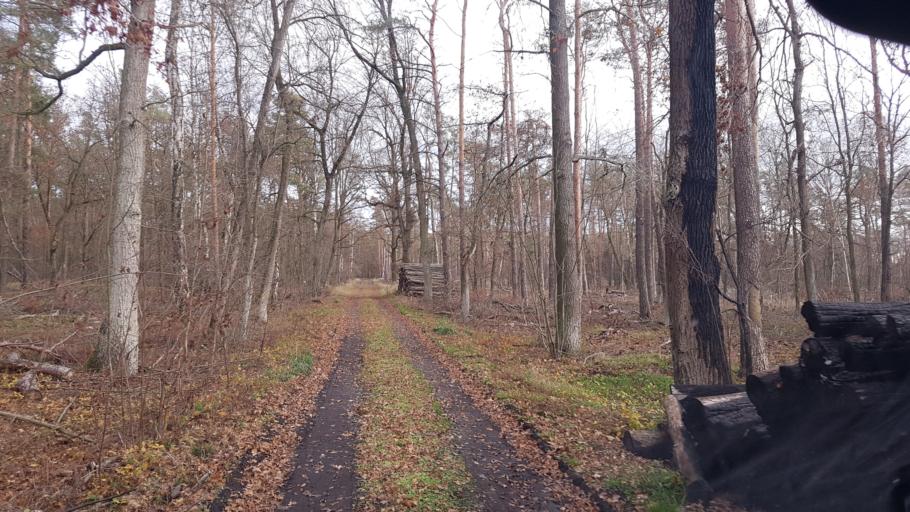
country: DE
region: Brandenburg
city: Falkenberg
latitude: 51.5625
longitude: 13.2843
